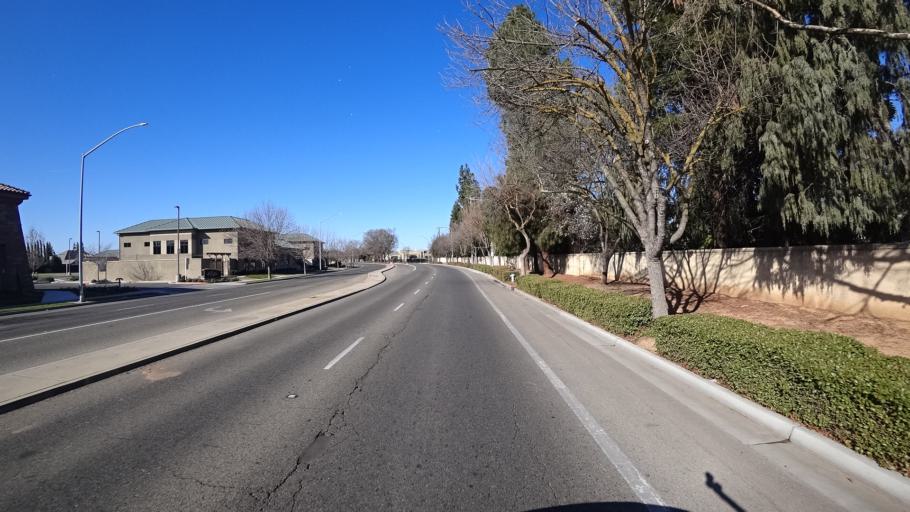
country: US
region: California
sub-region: Fresno County
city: West Park
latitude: 36.8300
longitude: -119.8643
